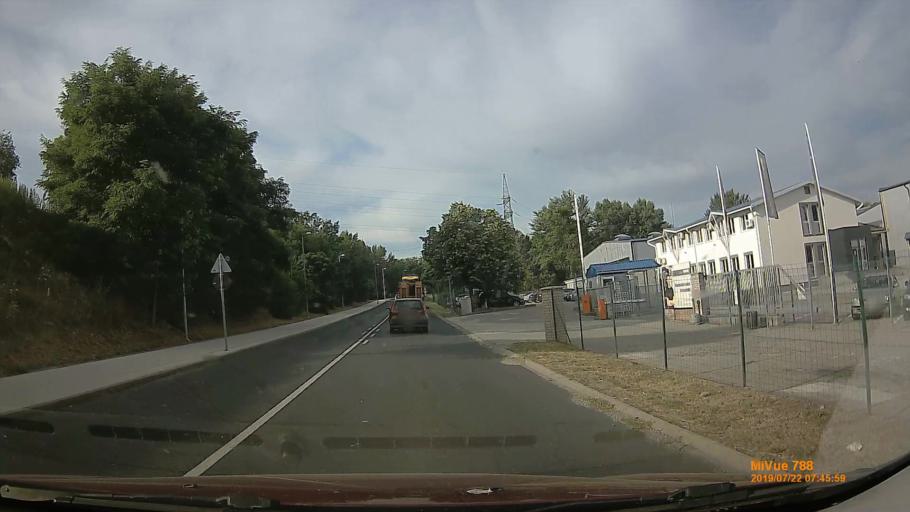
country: HU
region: Veszprem
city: Ajka
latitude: 47.0907
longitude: 17.5529
